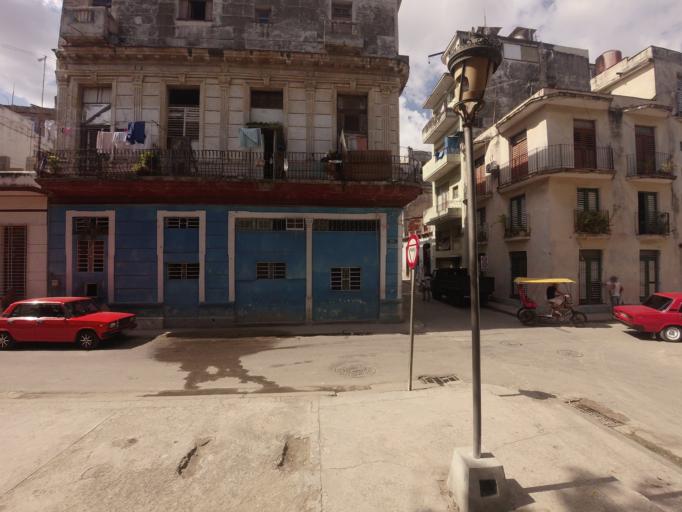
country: CU
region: La Habana
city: La Habana Vieja
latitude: 23.1295
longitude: -82.3530
